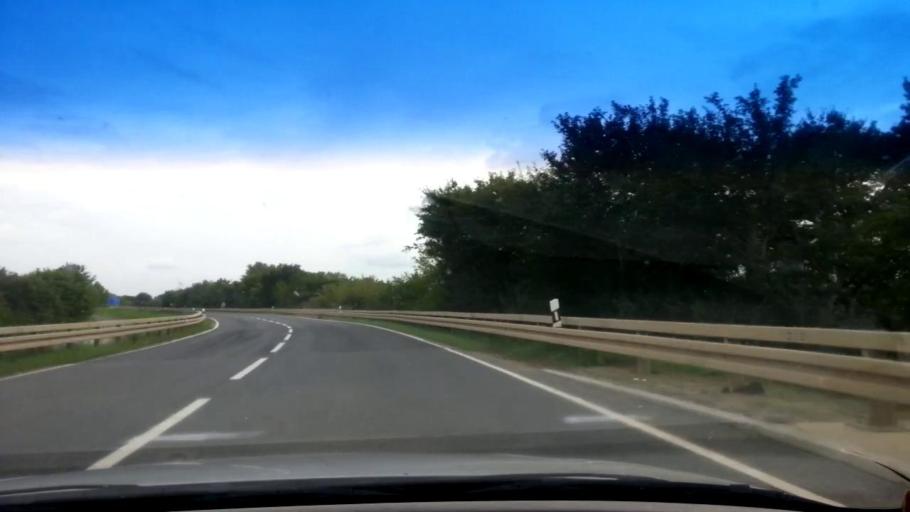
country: DE
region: Bavaria
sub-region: Upper Franconia
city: Breitengussbach
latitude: 49.9844
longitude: 10.8829
